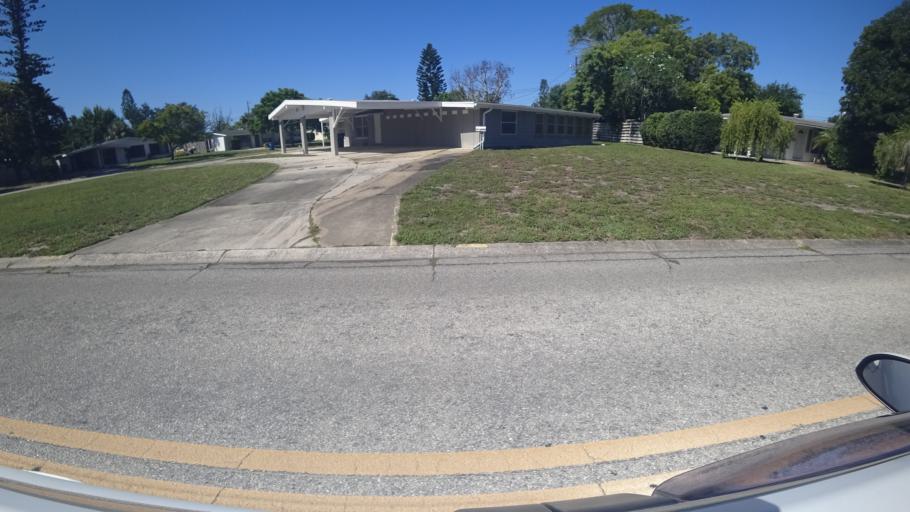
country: US
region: Florida
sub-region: Manatee County
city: Bayshore Gardens
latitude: 27.4245
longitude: -82.5941
